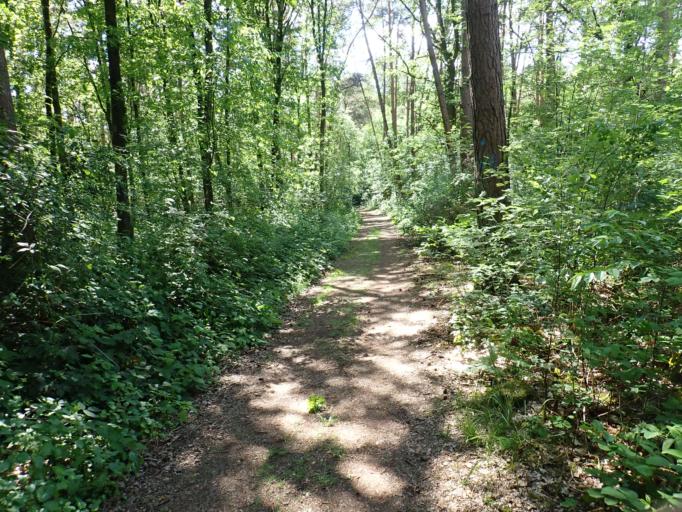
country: BE
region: Flanders
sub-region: Provincie Antwerpen
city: Kasterlee
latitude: 51.2250
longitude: 4.9379
